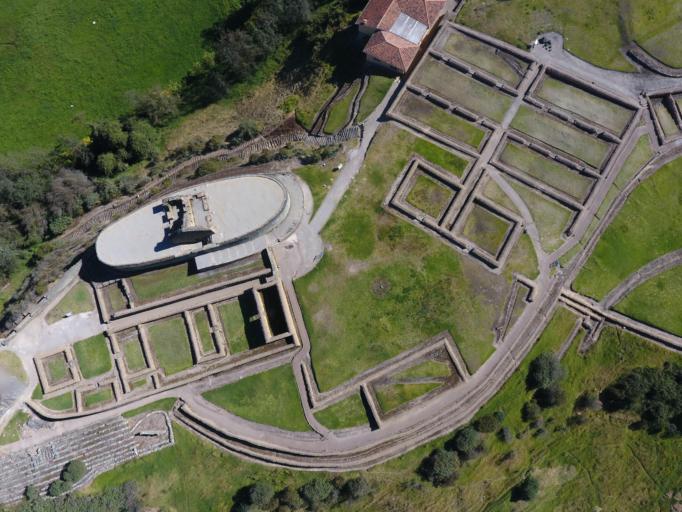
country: EC
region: Canar
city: Canar
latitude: -2.5400
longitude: -78.8747
